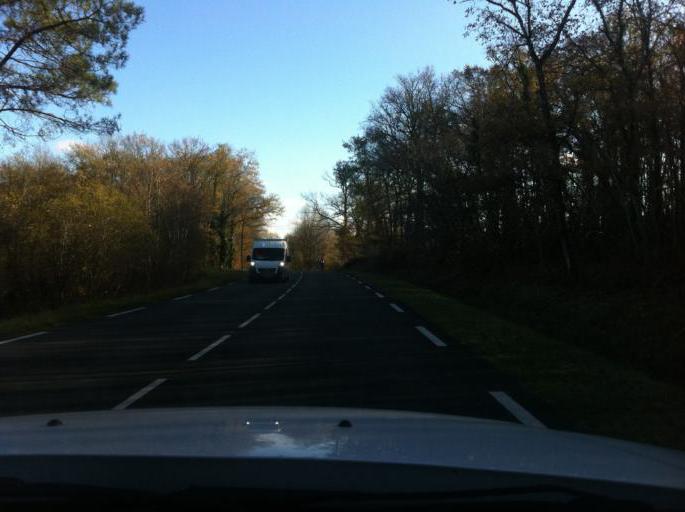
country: FR
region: Aquitaine
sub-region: Departement de la Dordogne
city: Rouffignac-Saint-Cernin-de-Reilhac
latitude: 45.0405
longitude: 0.8697
